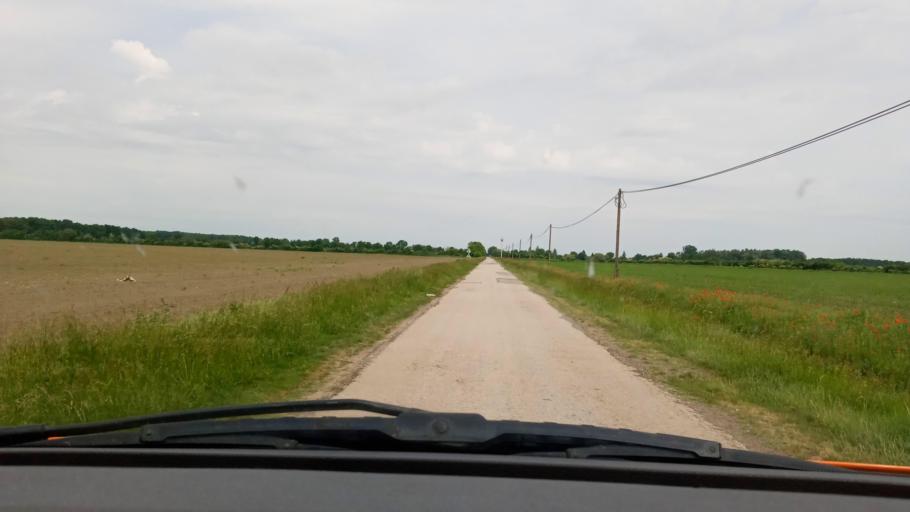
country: HU
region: Baranya
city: Vajszlo
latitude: 45.9176
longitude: 18.0254
